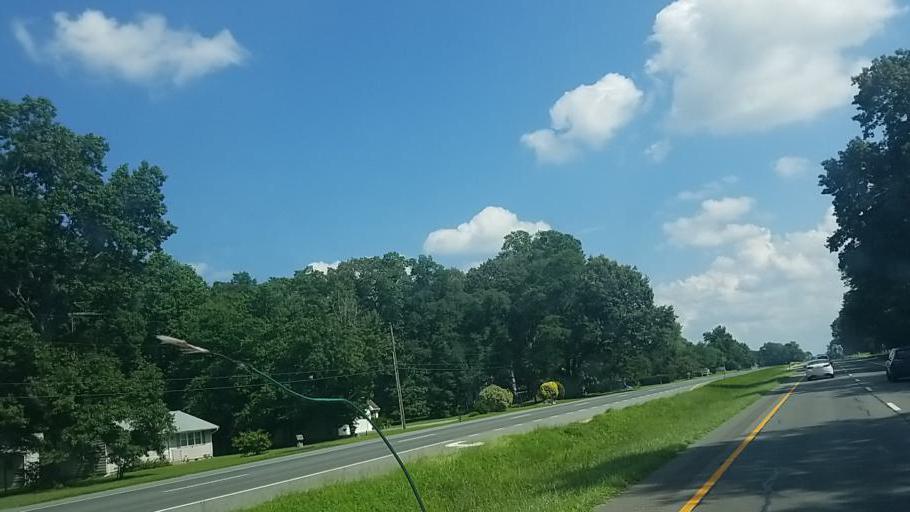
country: US
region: Delaware
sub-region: Sussex County
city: Georgetown
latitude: 38.6468
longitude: -75.3623
